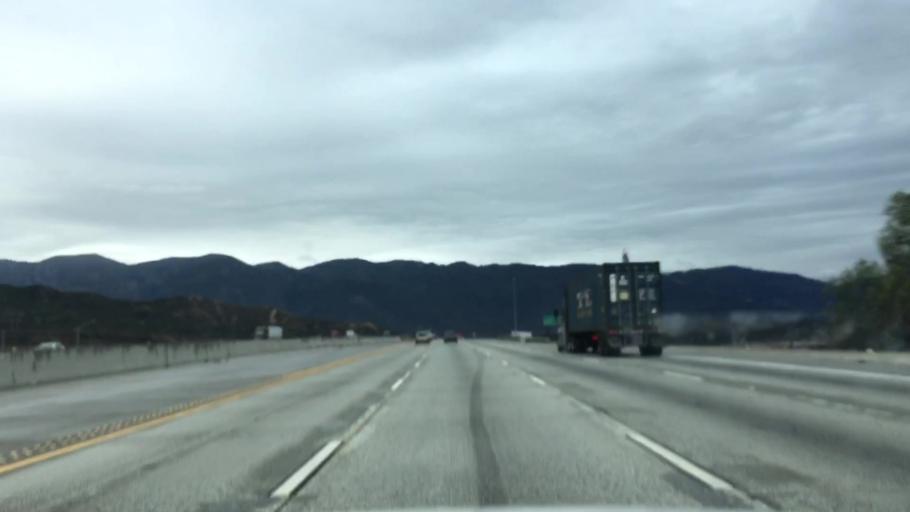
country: US
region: California
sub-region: San Bernardino County
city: Fontana
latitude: 34.1804
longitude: -117.4380
